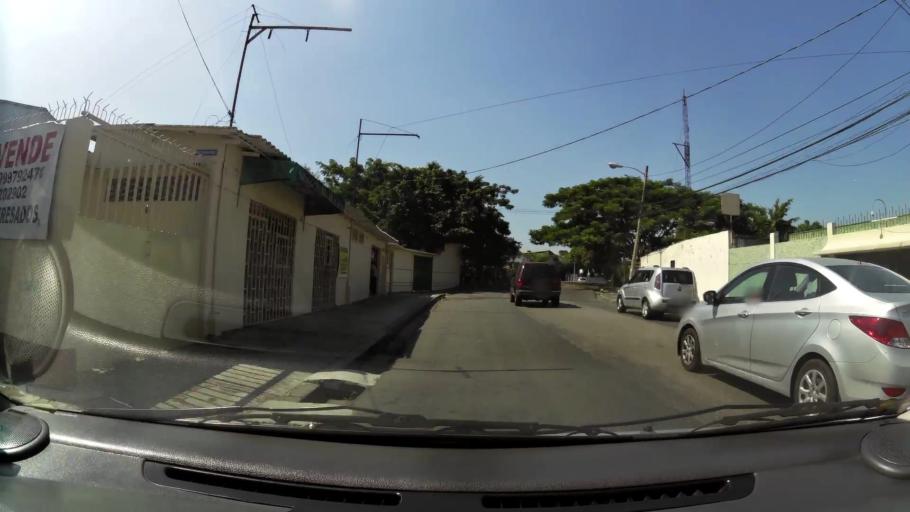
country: EC
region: Guayas
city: Guayaquil
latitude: -2.1636
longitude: -79.9178
